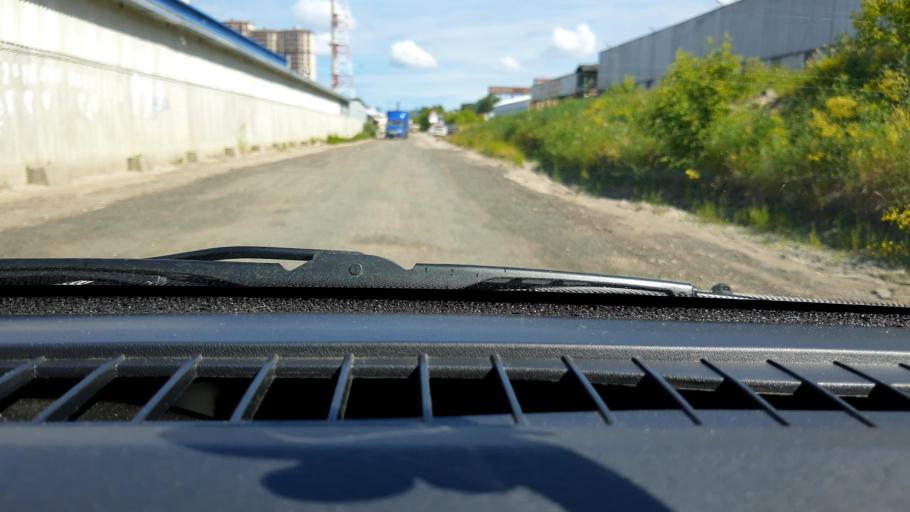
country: RU
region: Nizjnij Novgorod
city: Nizhniy Novgorod
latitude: 56.3040
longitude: 43.9481
